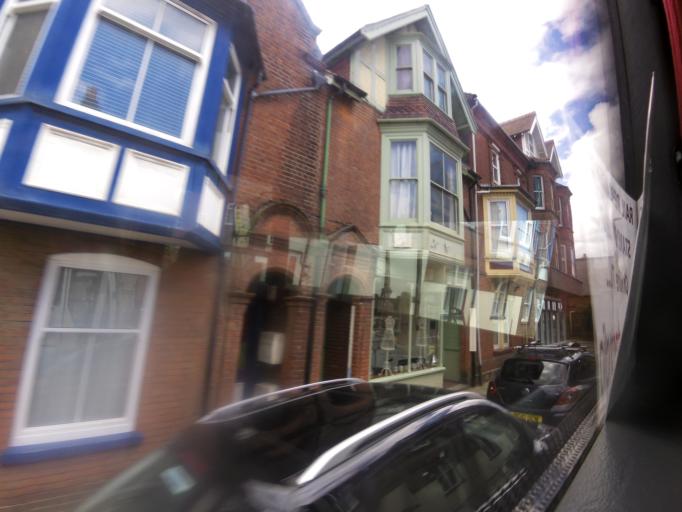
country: GB
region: England
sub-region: Norfolk
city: Cromer
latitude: 52.9301
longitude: 1.3017
